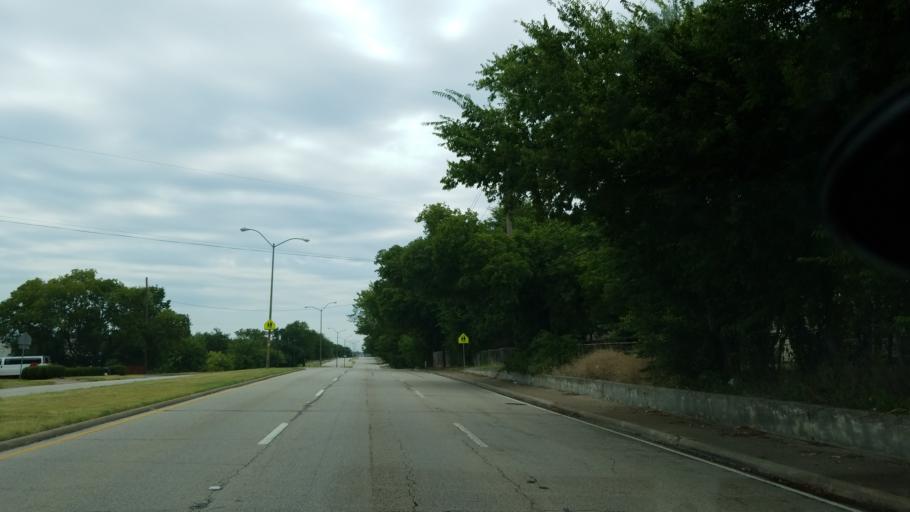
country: US
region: Texas
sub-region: Dallas County
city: DeSoto
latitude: 32.6547
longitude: -96.8400
